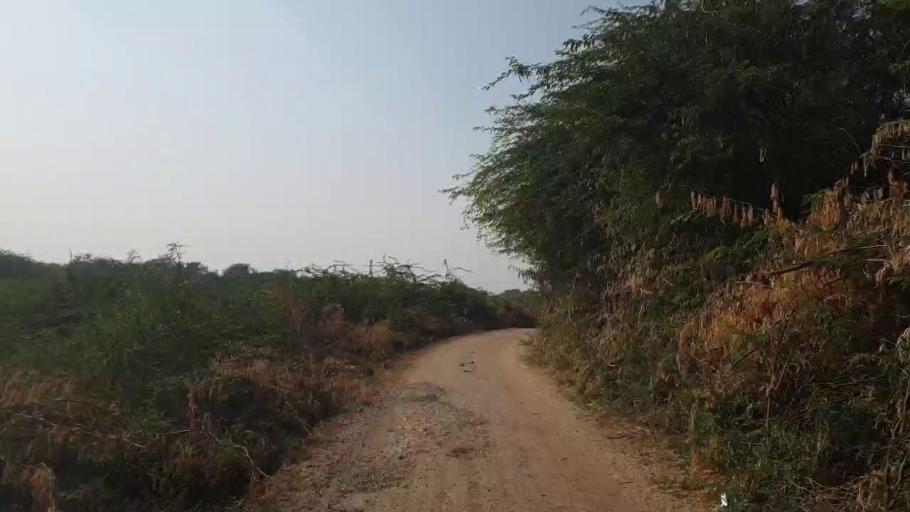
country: PK
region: Sindh
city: Kotri
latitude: 25.3105
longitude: 68.3003
